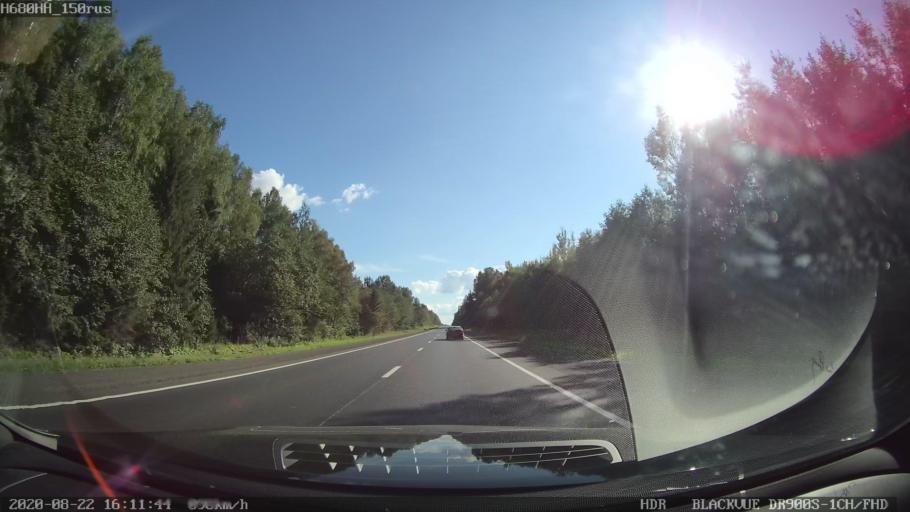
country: RU
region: Tverskaya
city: Rameshki
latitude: 57.4980
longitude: 36.2571
